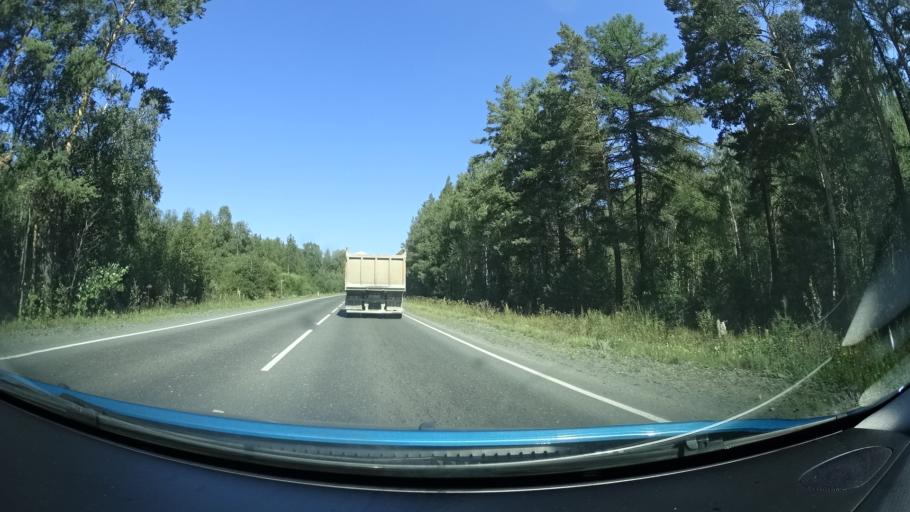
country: RU
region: Bashkortostan
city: Abzakovo
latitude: 53.8671
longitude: 58.5400
